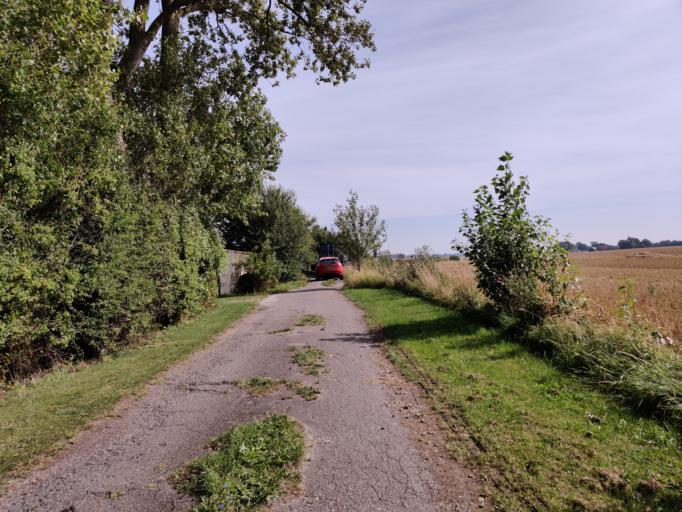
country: DK
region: Zealand
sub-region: Guldborgsund Kommune
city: Nykobing Falster
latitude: 54.6318
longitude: 11.9082
